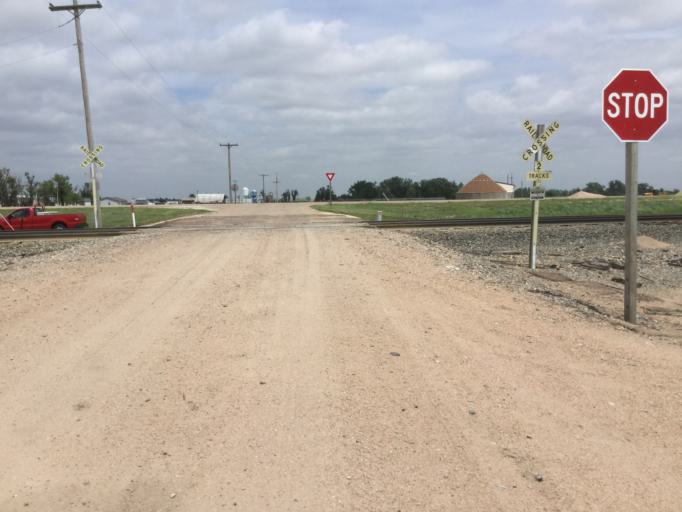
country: US
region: Kansas
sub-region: Edwards County
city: Kinsley
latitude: 37.9116
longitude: -99.4417
